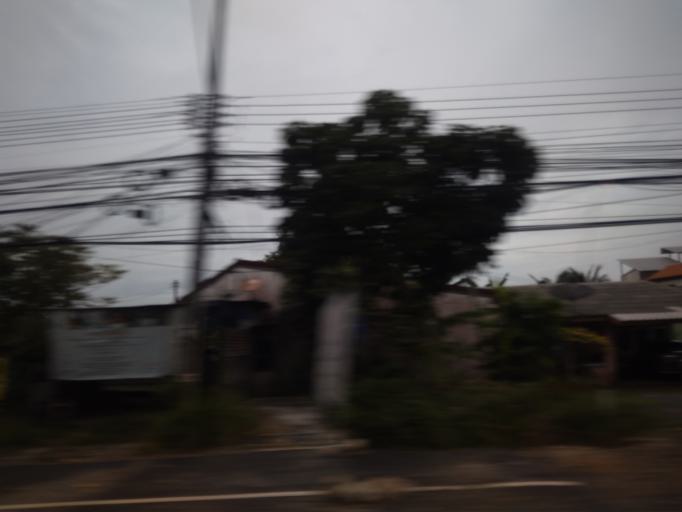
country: TH
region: Phuket
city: Mueang Phuket
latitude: 7.8385
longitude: 98.3926
